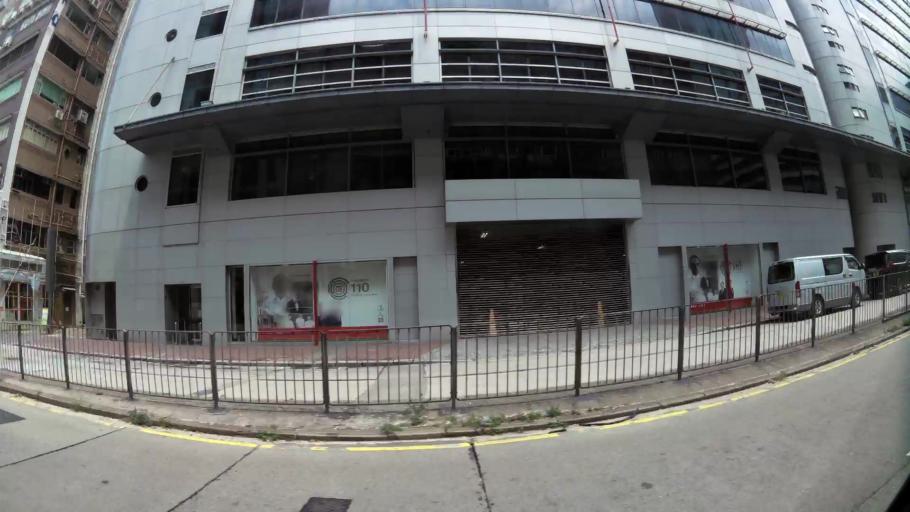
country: HK
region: Sham Shui Po
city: Sham Shui Po
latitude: 22.3371
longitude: 114.1471
